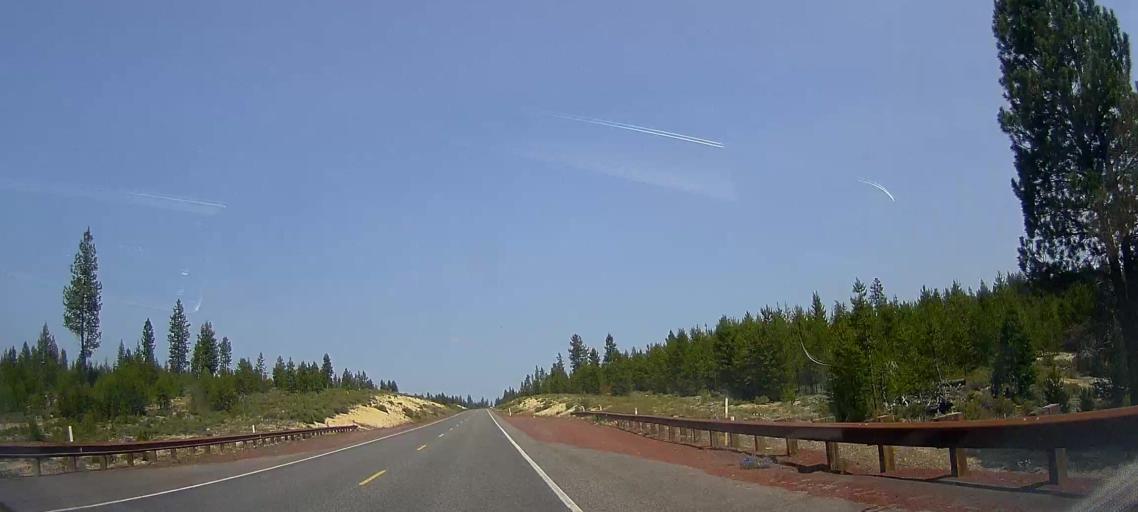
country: US
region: Oregon
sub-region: Deschutes County
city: La Pine
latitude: 43.4008
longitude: -121.7249
